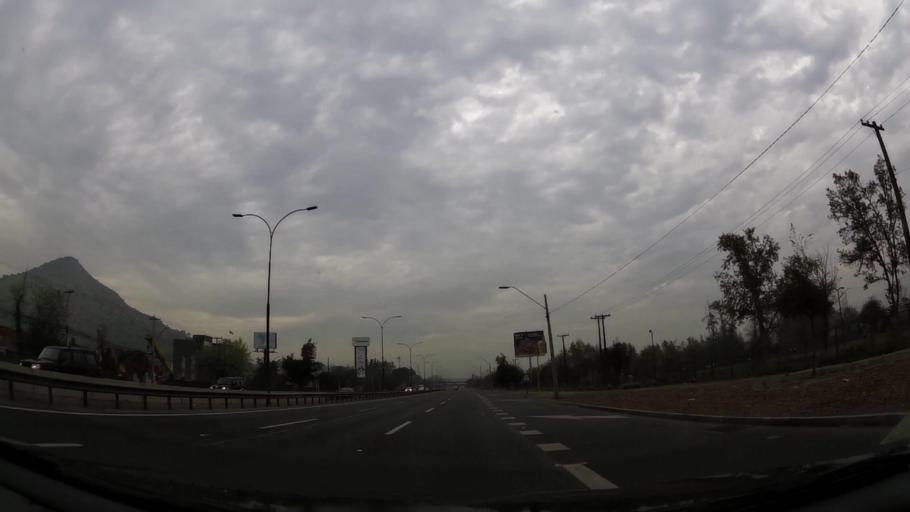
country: CL
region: Santiago Metropolitan
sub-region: Provincia de Santiago
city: Lo Prado
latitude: -33.3860
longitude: -70.6912
